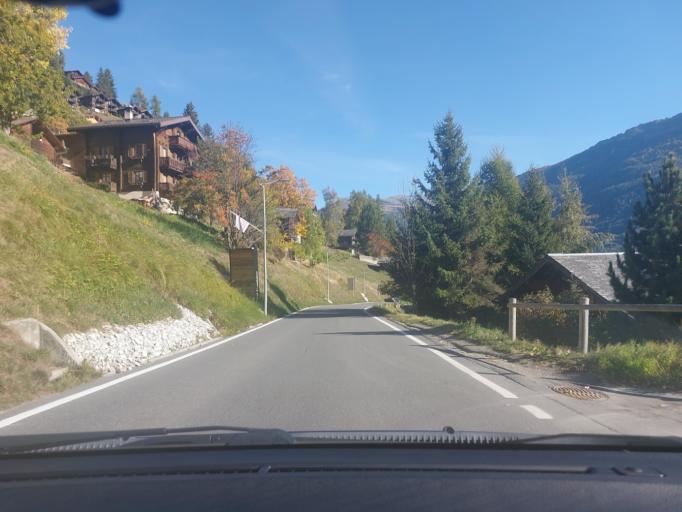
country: CH
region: Valais
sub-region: Sierre District
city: Chippis
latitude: 46.1815
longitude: 7.5770
